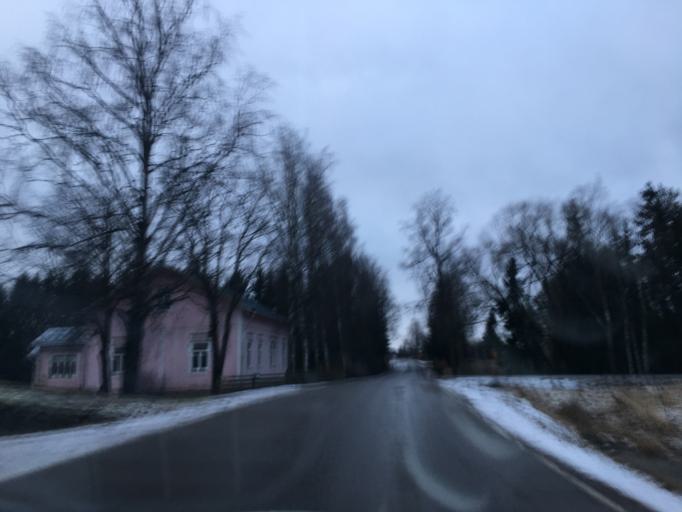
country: FI
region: Varsinais-Suomi
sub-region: Loimaa
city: Aura
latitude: 60.6260
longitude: 22.5835
